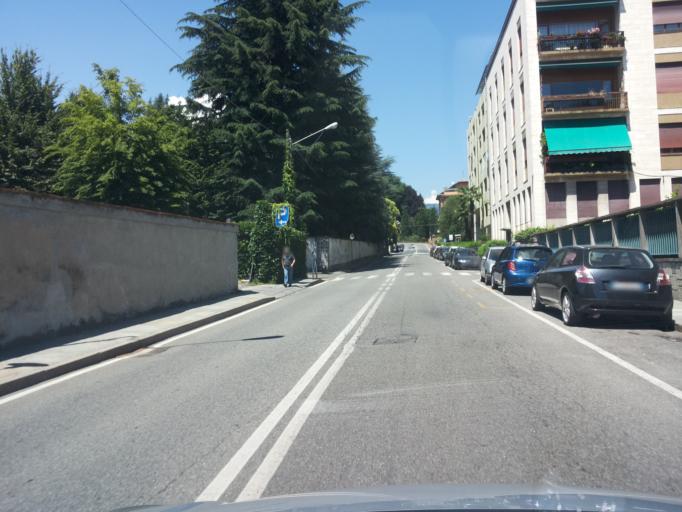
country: IT
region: Piedmont
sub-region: Provincia di Biella
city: Biella
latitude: 45.5705
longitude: 8.0504
